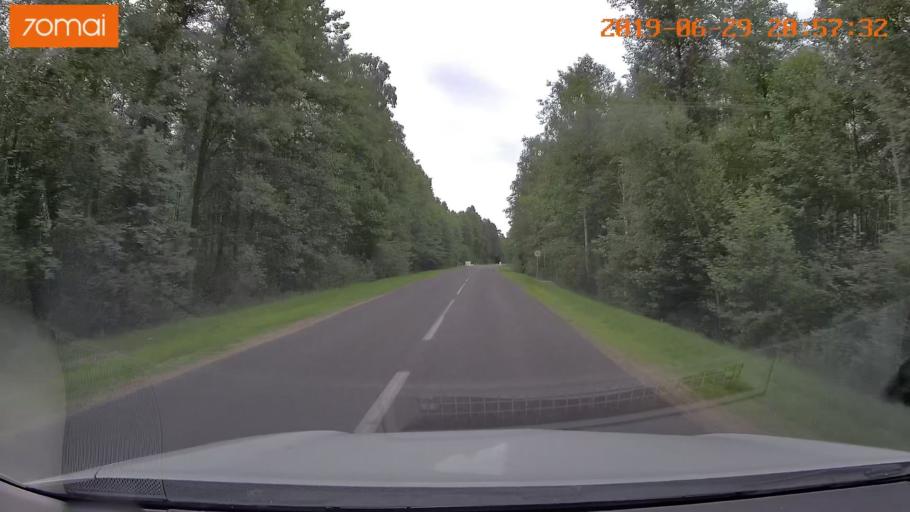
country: BY
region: Brest
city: Hantsavichy
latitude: 52.7203
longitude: 26.3716
